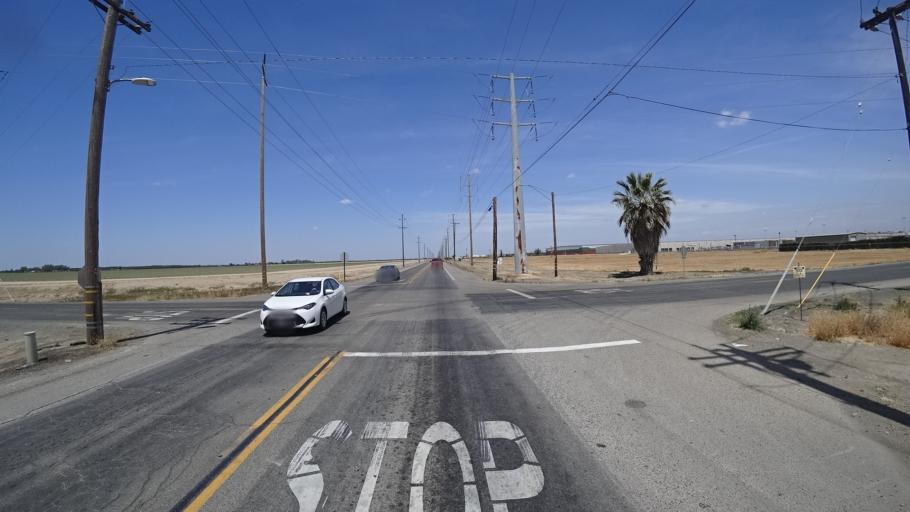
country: US
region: California
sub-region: Kings County
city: Home Garden
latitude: 36.2546
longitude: -119.6549
